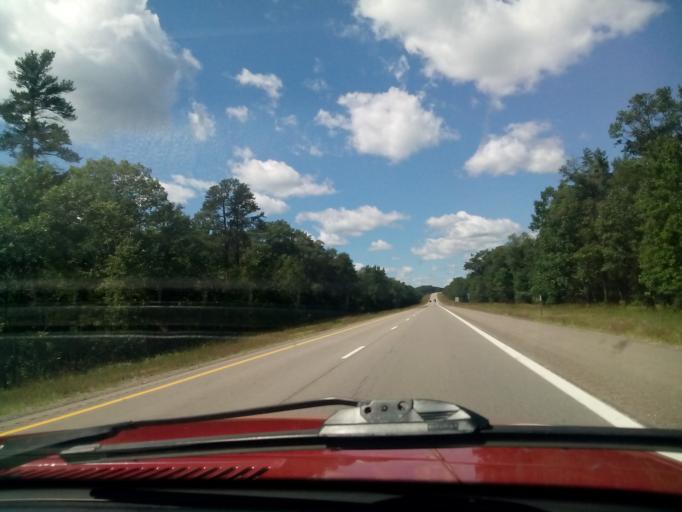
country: US
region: Michigan
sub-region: Roscommon County
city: Roscommon
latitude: 44.4786
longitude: -84.6250
